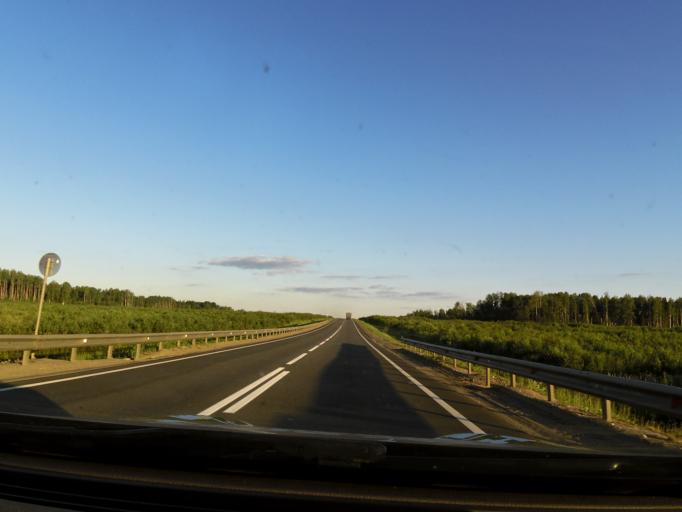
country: RU
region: Vologda
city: Gryazovets
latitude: 58.6563
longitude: 40.3171
